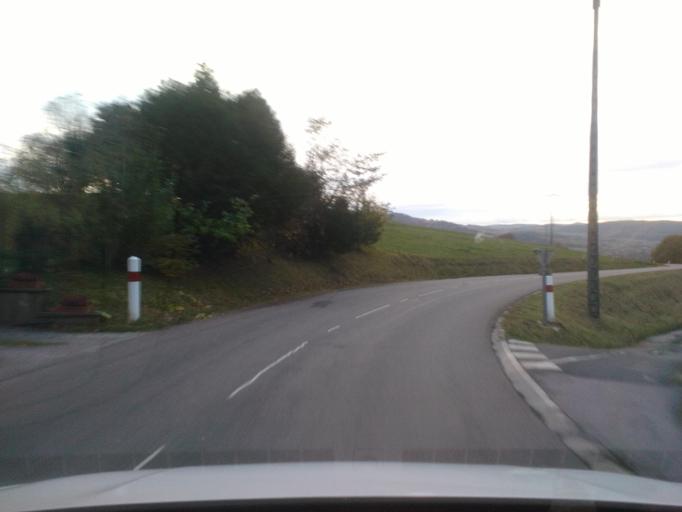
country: FR
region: Lorraine
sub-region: Departement des Vosges
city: Plainfaing
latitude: 48.1915
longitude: 7.0174
